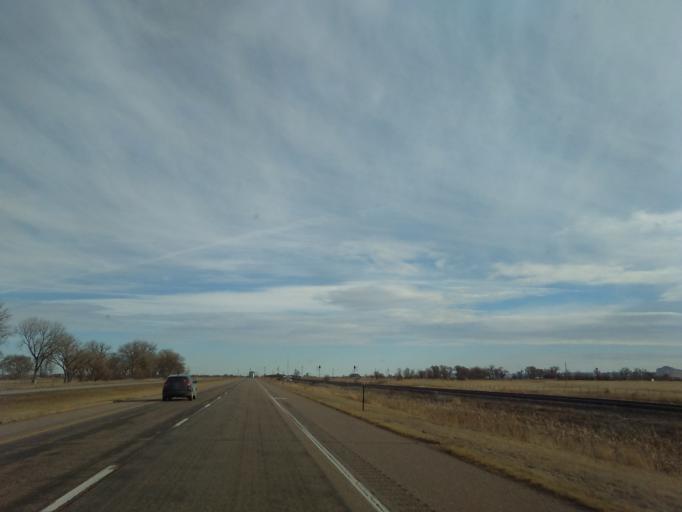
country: US
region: Nebraska
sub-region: Scotts Bluff County
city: Gering
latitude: 41.8210
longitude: -103.5455
